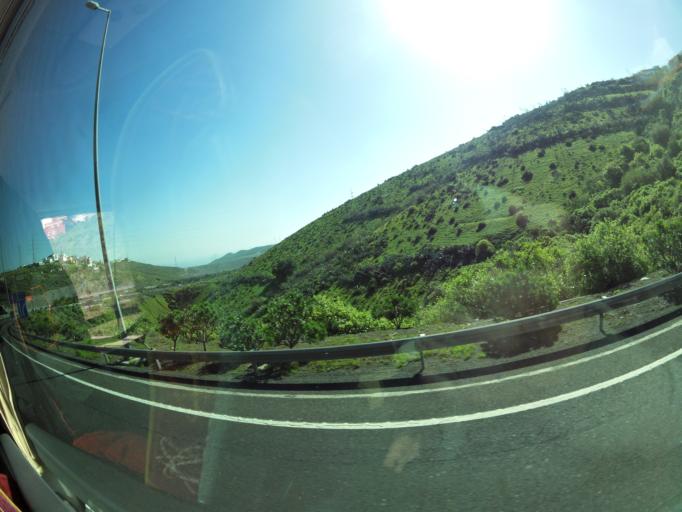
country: ES
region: Canary Islands
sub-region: Provincia de Las Palmas
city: Las Palmas de Gran Canaria
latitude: 28.0555
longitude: -15.4439
